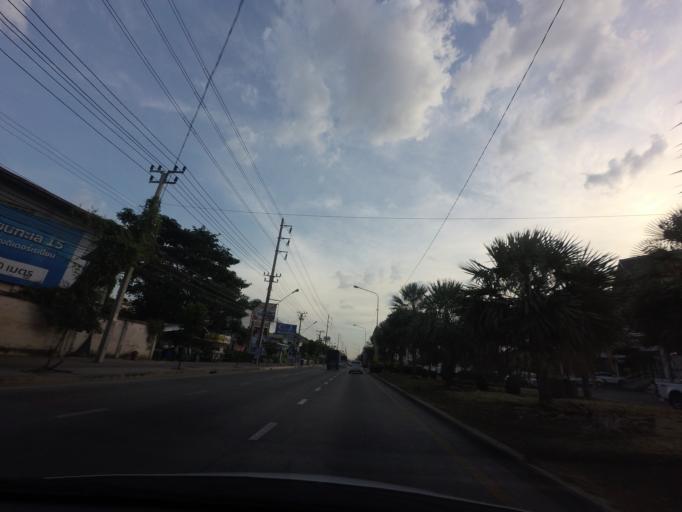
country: TH
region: Bangkok
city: Bang Khun Thian
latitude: 13.6391
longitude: 100.4327
